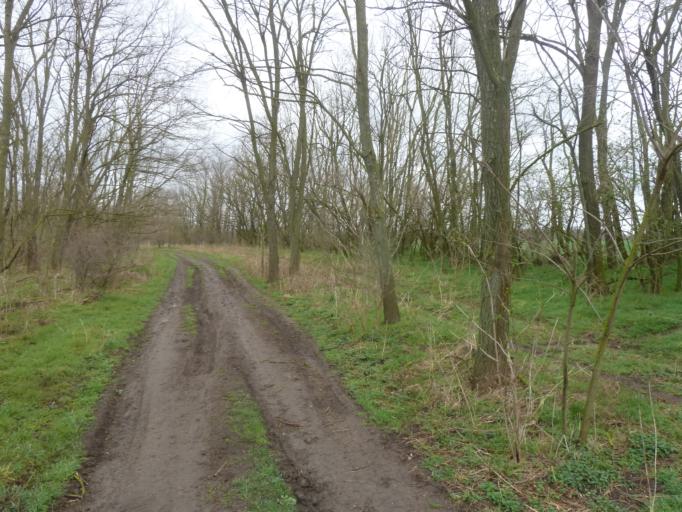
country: HU
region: Gyor-Moson-Sopron
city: Fertoszentmiklos
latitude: 47.4826
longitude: 16.8213
